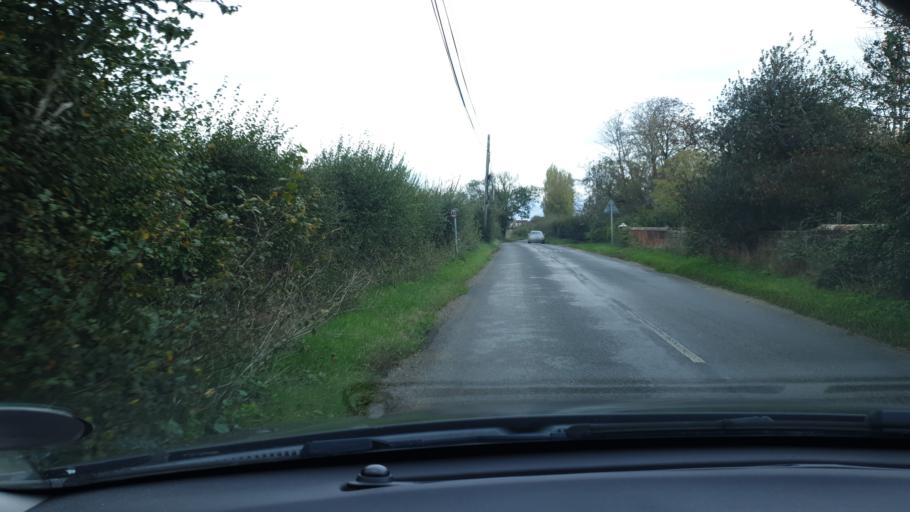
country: GB
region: England
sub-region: Essex
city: Mistley
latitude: 51.9370
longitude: 1.0948
